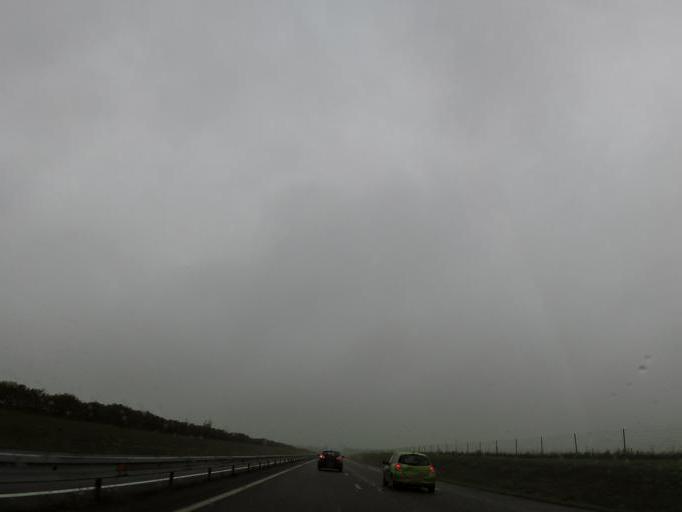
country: FR
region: Champagne-Ardenne
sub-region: Departement de la Marne
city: Courtisols
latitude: 49.0356
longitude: 4.6050
